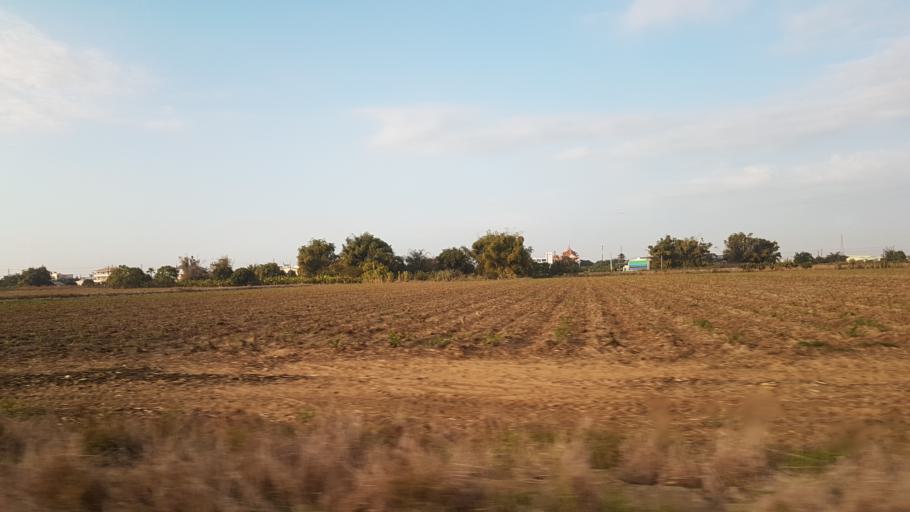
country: TW
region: Taiwan
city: Xinying
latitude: 23.3472
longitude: 120.3683
